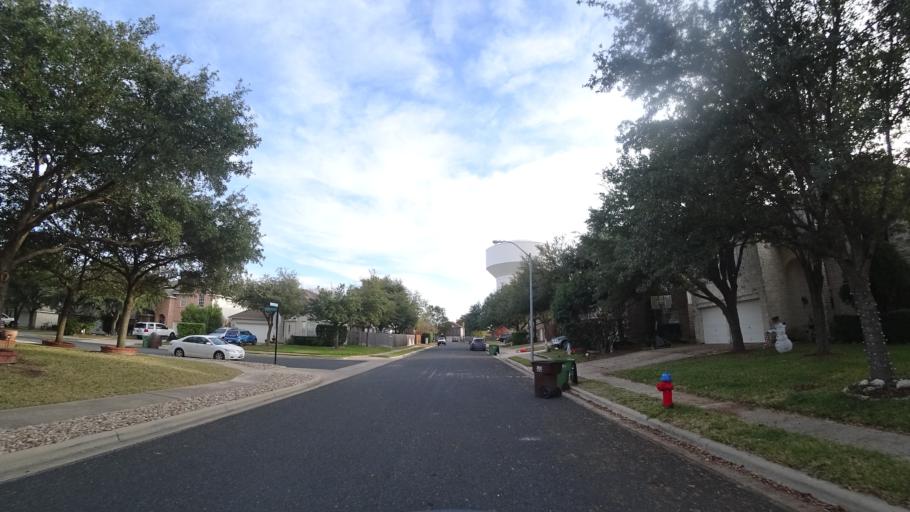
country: US
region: Texas
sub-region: Williamson County
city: Brushy Creek
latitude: 30.5119
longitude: -97.7308
